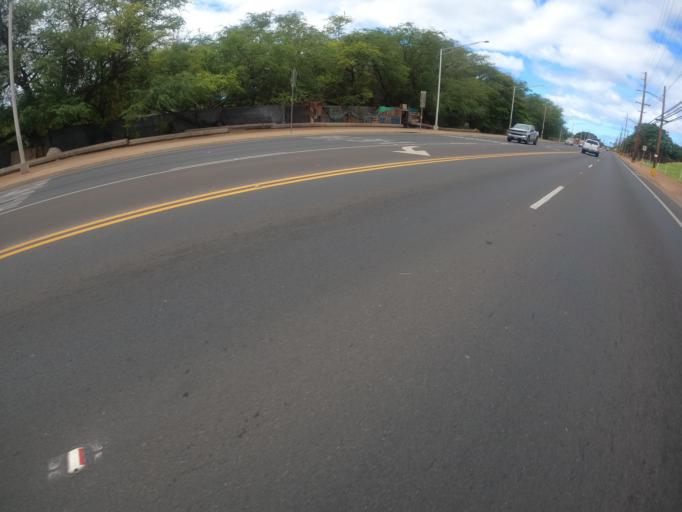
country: US
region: Hawaii
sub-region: Honolulu County
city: Waianae
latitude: 21.4535
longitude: -158.1960
